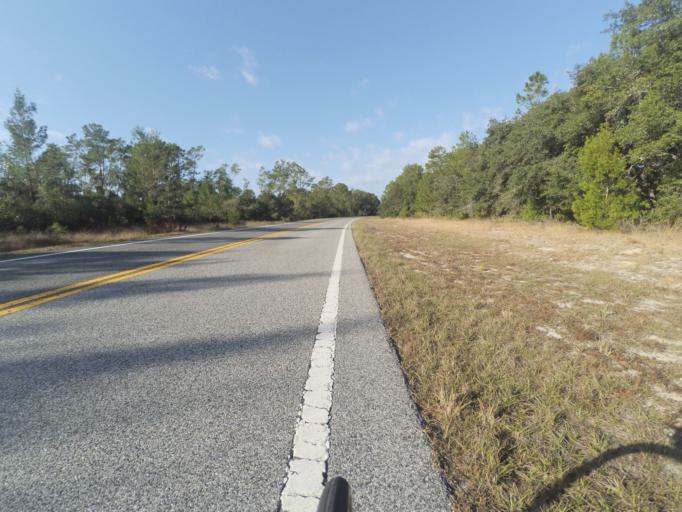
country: US
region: Florida
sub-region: Lake County
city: Astor
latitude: 29.1427
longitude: -81.5863
